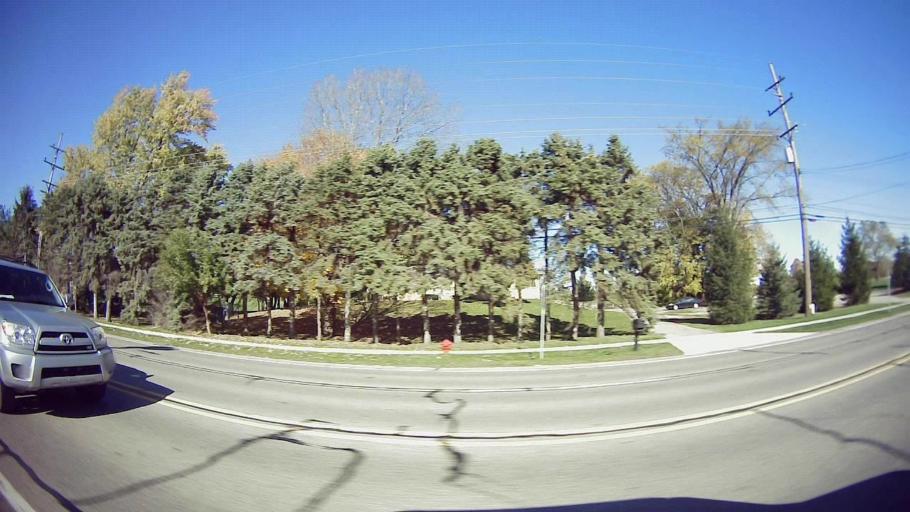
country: US
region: Michigan
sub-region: Oakland County
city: Bingham Farms
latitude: 42.5450
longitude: -83.2736
